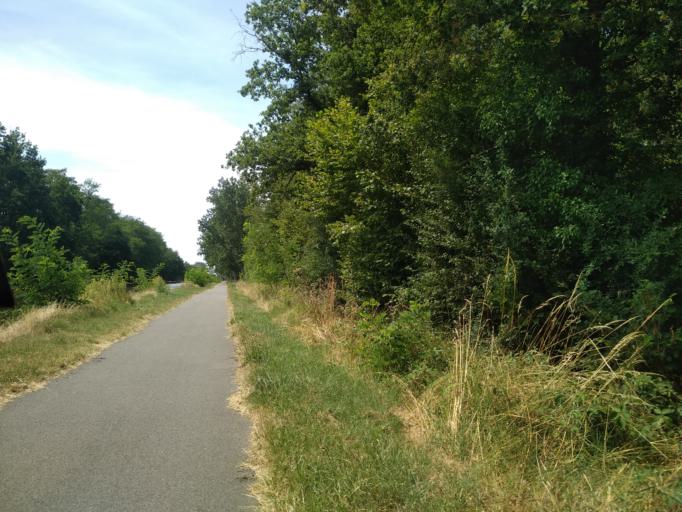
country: FR
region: Auvergne
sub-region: Departement de l'Allier
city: Molinet
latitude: 46.4788
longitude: 3.9058
